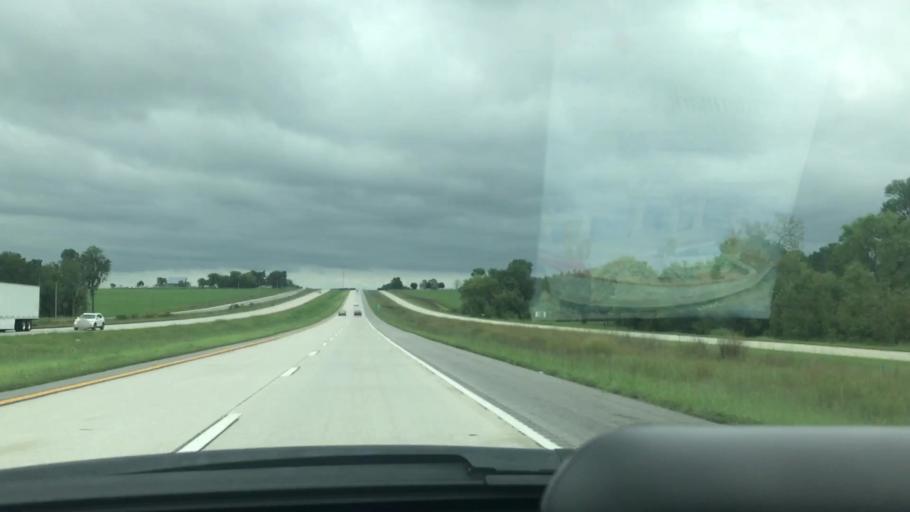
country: US
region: Missouri
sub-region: Greene County
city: Fair Grove
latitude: 37.4290
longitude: -93.1449
